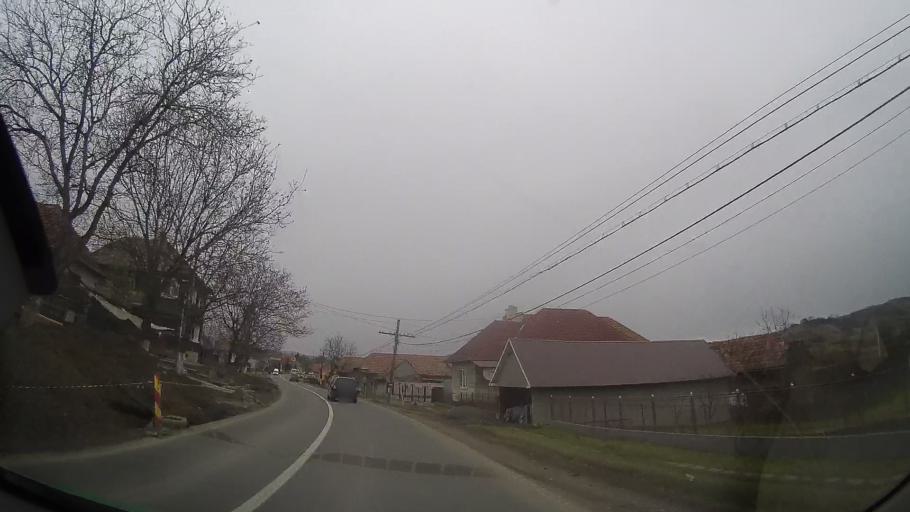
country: RO
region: Mures
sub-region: Comuna Ceausu de Campie
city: Ceausu de Campie
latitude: 46.6111
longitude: 24.5284
